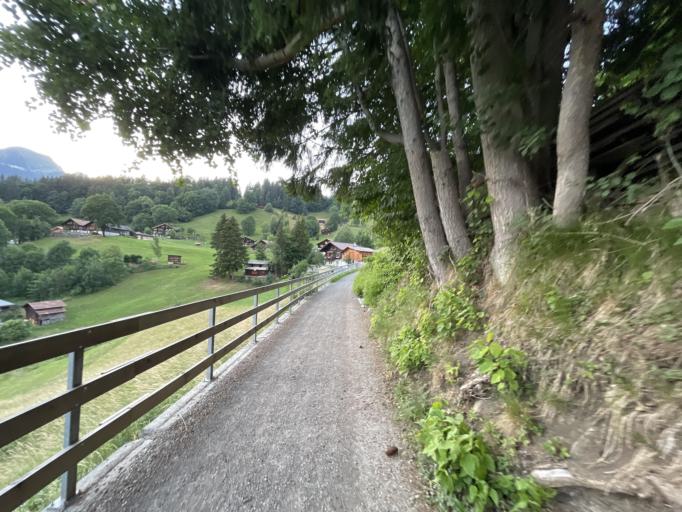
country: CH
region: Bern
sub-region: Interlaken-Oberhasli District
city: Lauterbrunnen
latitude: 46.6104
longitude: 7.9124
